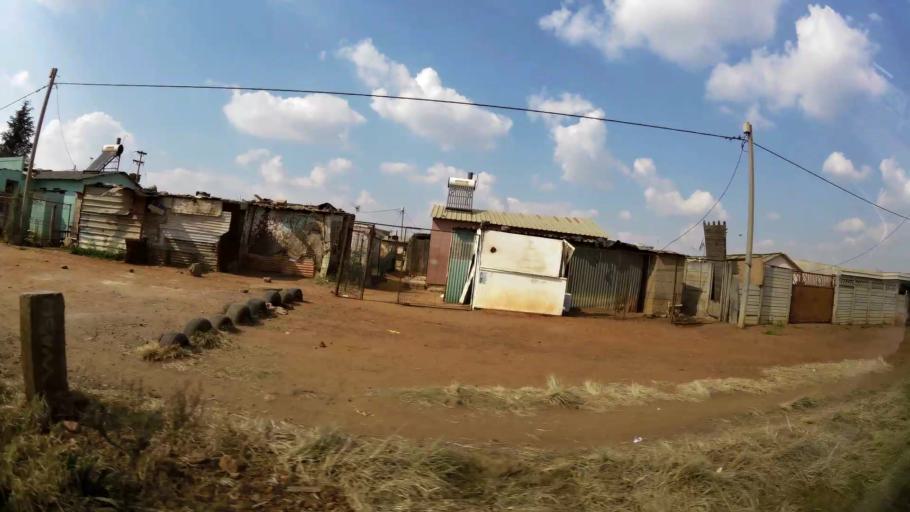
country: ZA
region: Gauteng
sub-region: Ekurhuleni Metropolitan Municipality
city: Springs
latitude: -26.1241
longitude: 28.4777
